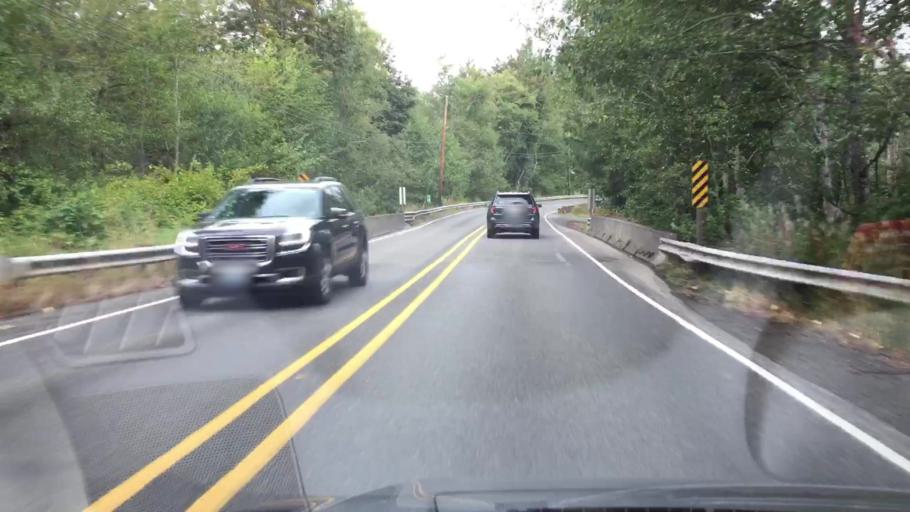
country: US
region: Washington
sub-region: Pierce County
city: Eatonville
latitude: 46.8478
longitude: -122.2541
